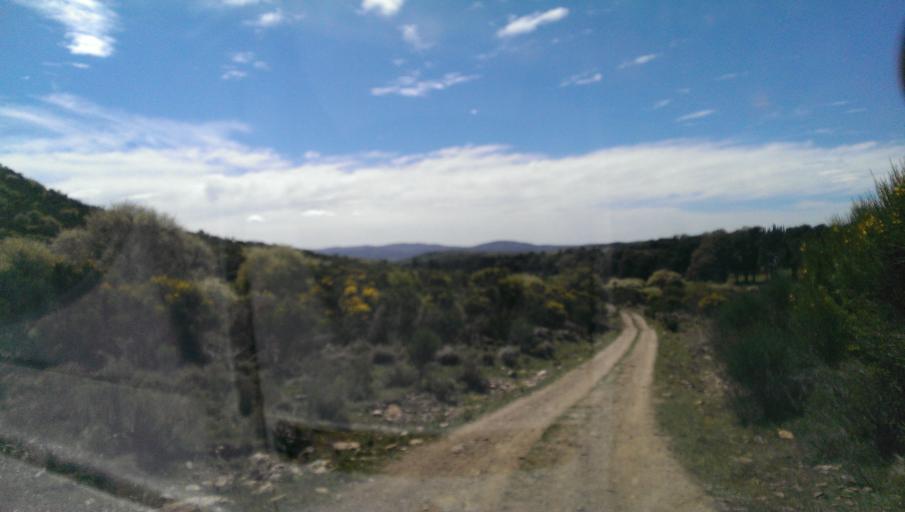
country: AR
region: Buenos Aires
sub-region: Partido de Tornquist
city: Tornquist
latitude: -38.1036
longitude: -61.9479
